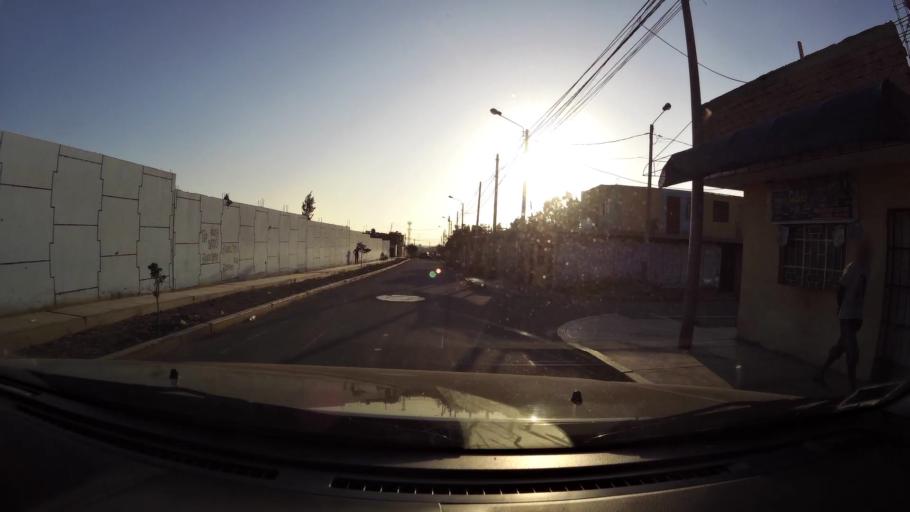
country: PE
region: Ica
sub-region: Provincia de Pisco
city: Villa Tupac Amaru
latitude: -13.7091
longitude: -76.1471
